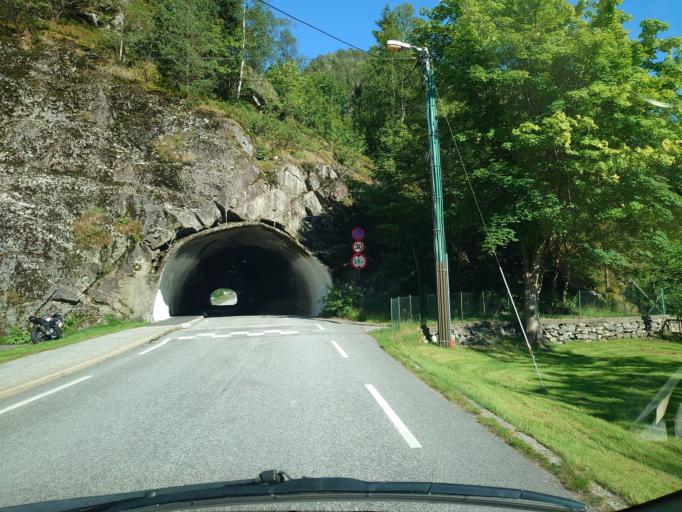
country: NO
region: Hordaland
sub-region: Vaksdal
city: Dale
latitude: 60.5900
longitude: 5.8245
